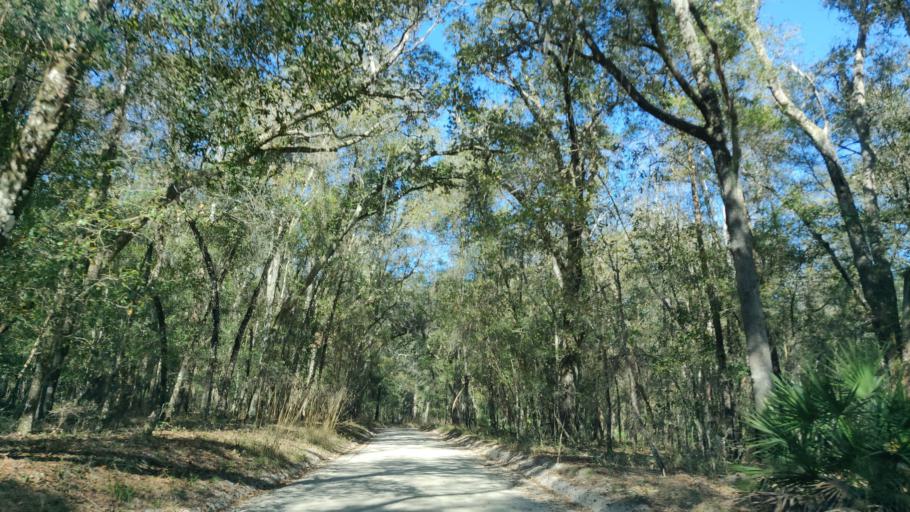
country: US
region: Florida
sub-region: Clay County
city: Middleburg
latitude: 30.1542
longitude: -81.9329
